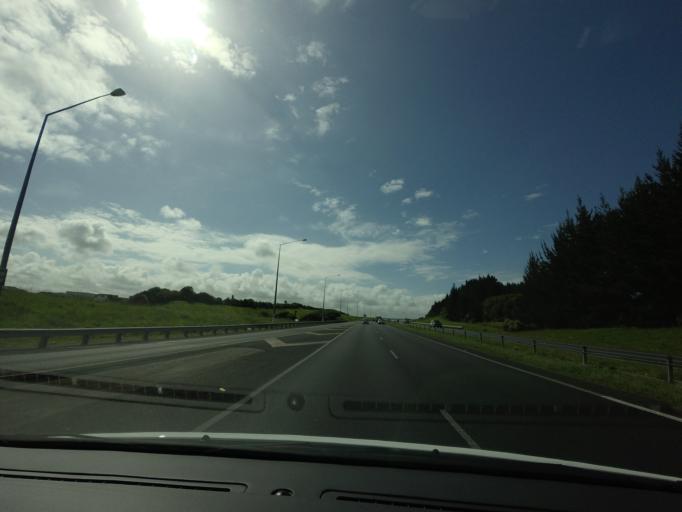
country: NZ
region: Auckland
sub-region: Auckland
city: Rothesay Bay
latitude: -36.6559
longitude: 174.6650
